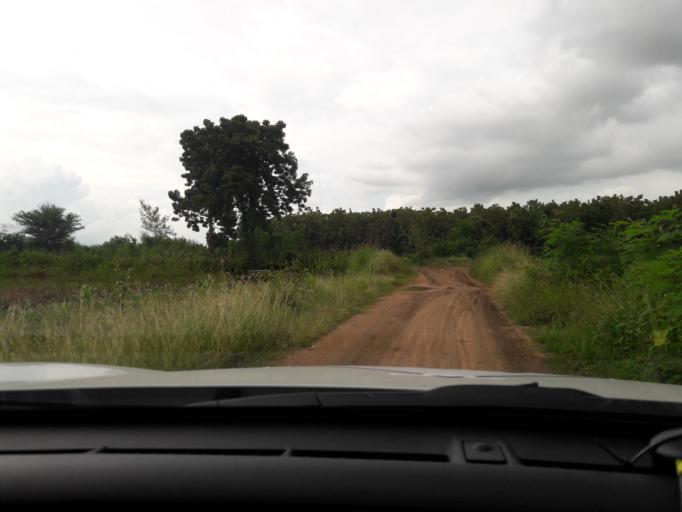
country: TH
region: Nakhon Sawan
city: Tak Fa
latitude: 15.3583
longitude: 100.4948
